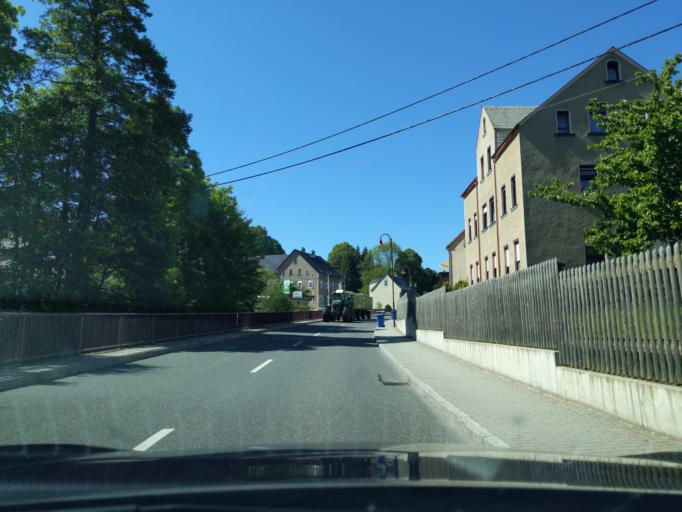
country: DE
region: Saxony
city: Stutzengrun
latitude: 50.5695
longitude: 12.5340
